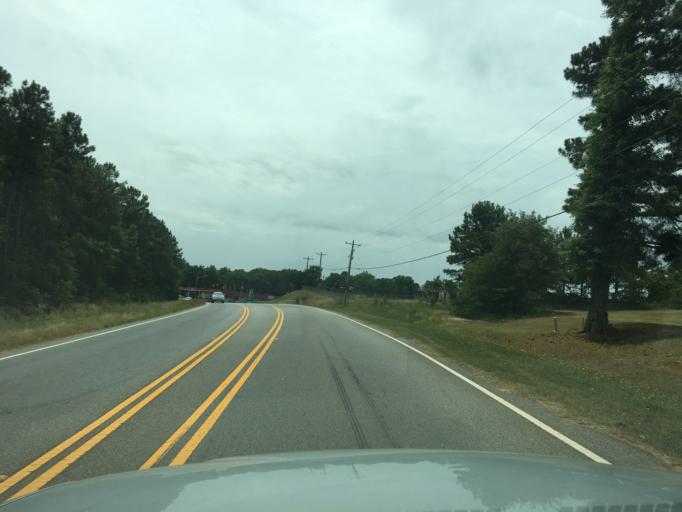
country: US
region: South Carolina
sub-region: Anderson County
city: Centerville
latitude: 34.5315
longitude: -82.8033
